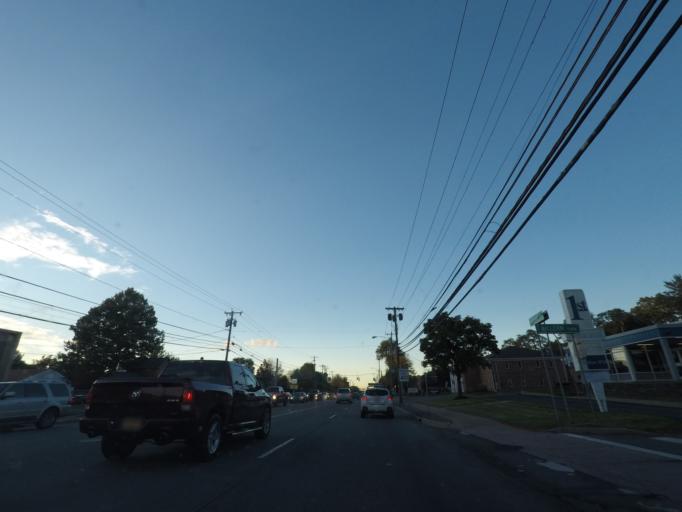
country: US
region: New York
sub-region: Albany County
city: Colonie
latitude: 42.7236
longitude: -73.8396
